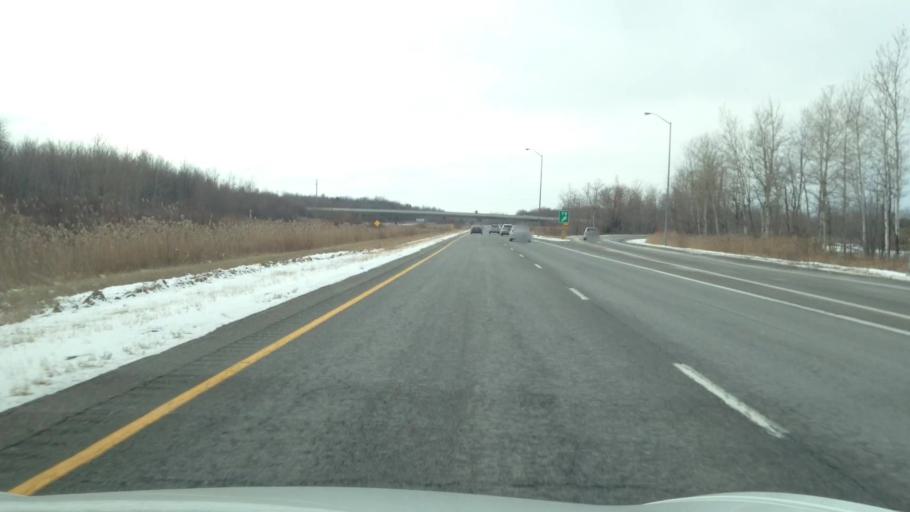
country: CA
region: Ontario
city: Bourget
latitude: 45.3142
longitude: -75.2362
